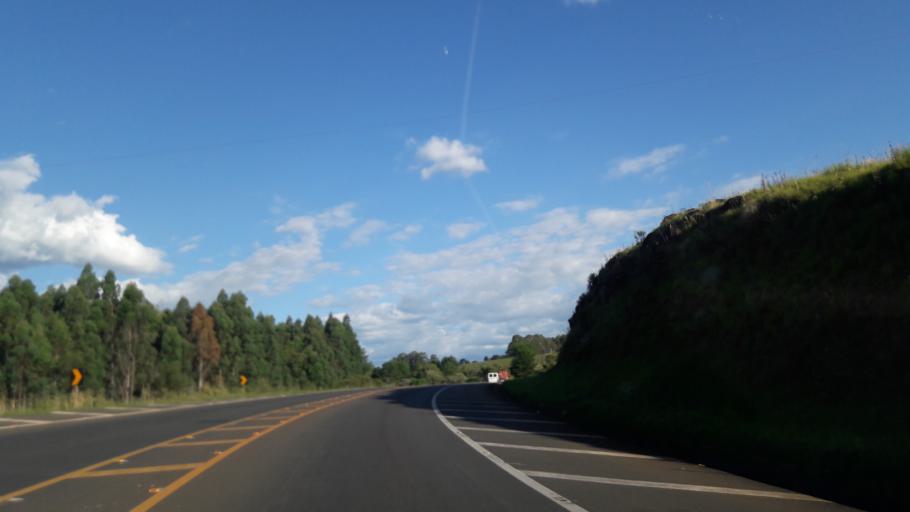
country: BR
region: Parana
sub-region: Guarapuava
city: Guarapuava
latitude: -25.3662
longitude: -51.3418
